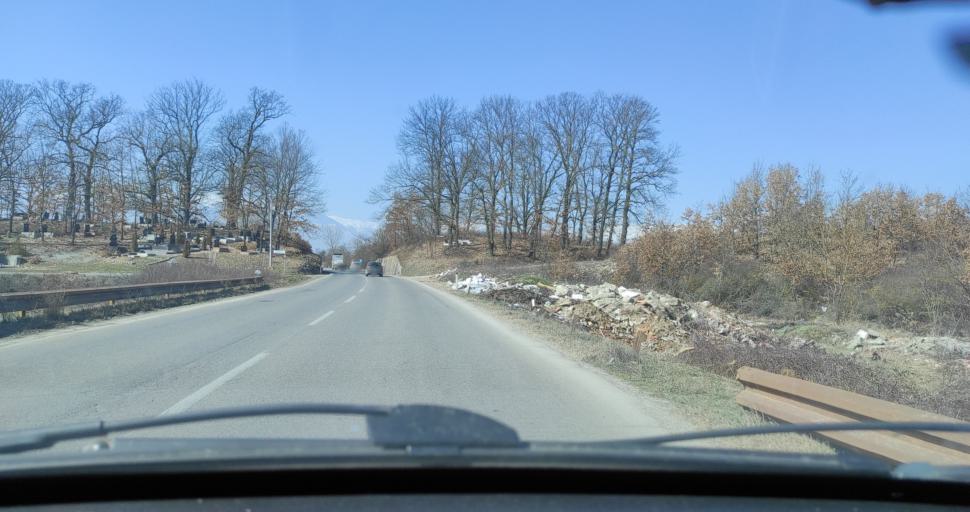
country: XK
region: Pec
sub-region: Komuna e Pejes
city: Kosuriq
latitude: 42.6201
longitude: 20.4850
